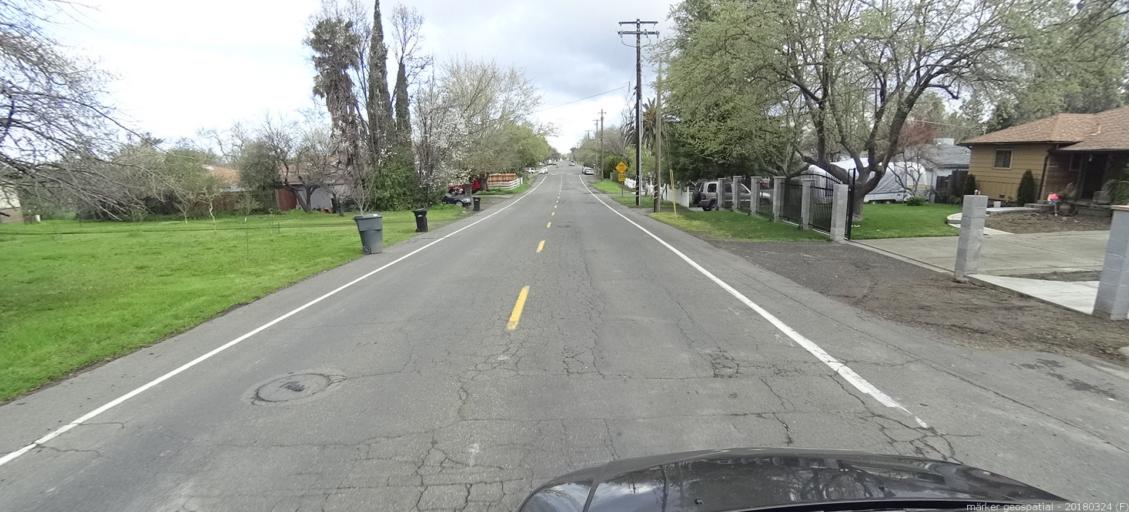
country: US
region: California
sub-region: Sacramento County
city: North Highlands
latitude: 38.6546
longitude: -121.3737
